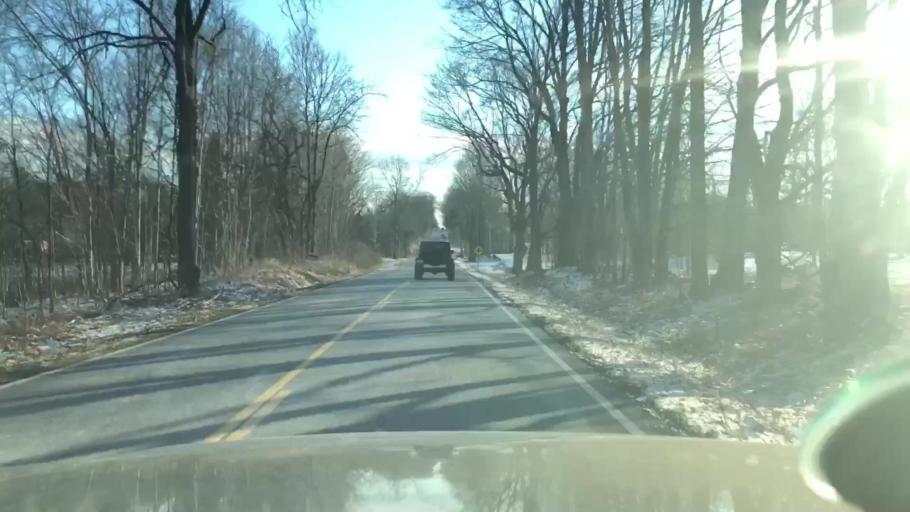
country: US
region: Michigan
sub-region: Jackson County
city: Vandercook Lake
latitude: 42.1327
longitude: -84.4516
